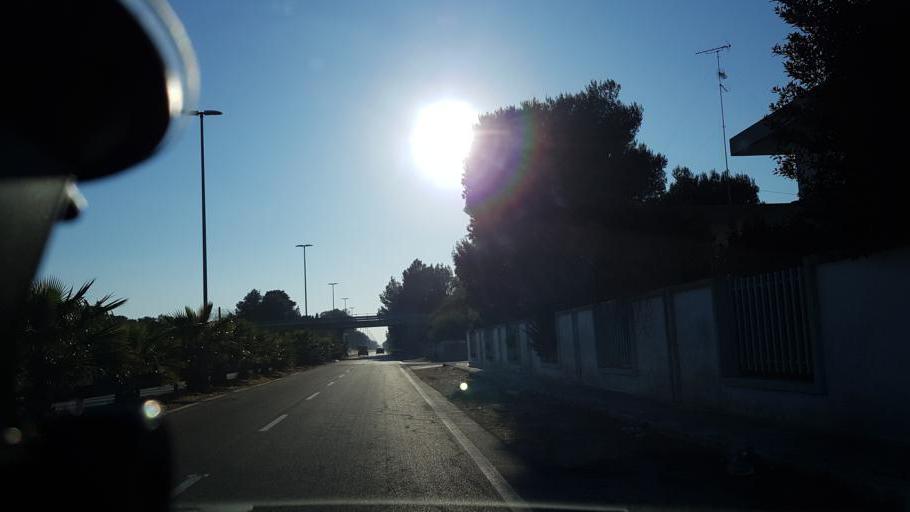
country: IT
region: Apulia
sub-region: Provincia di Lecce
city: Struda
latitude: 40.3881
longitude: 18.2980
